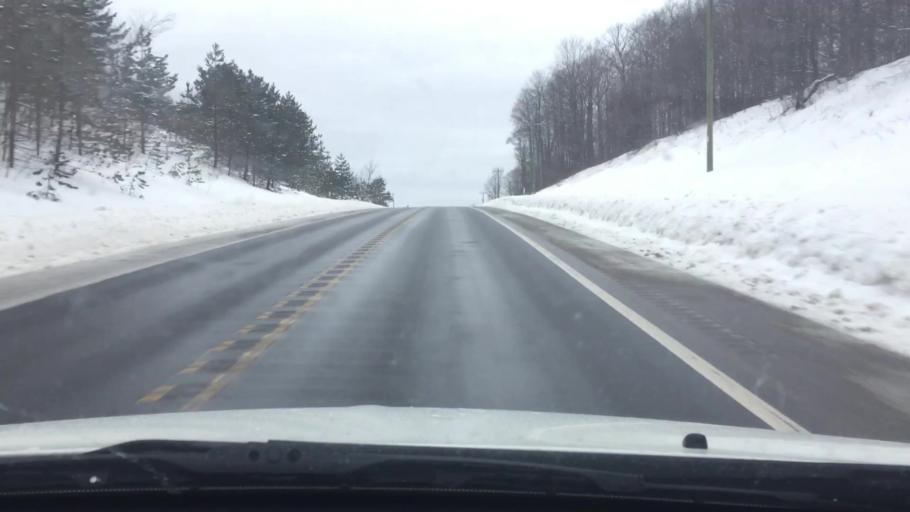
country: US
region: Michigan
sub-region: Charlevoix County
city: Boyne City
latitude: 45.0964
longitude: -85.0106
